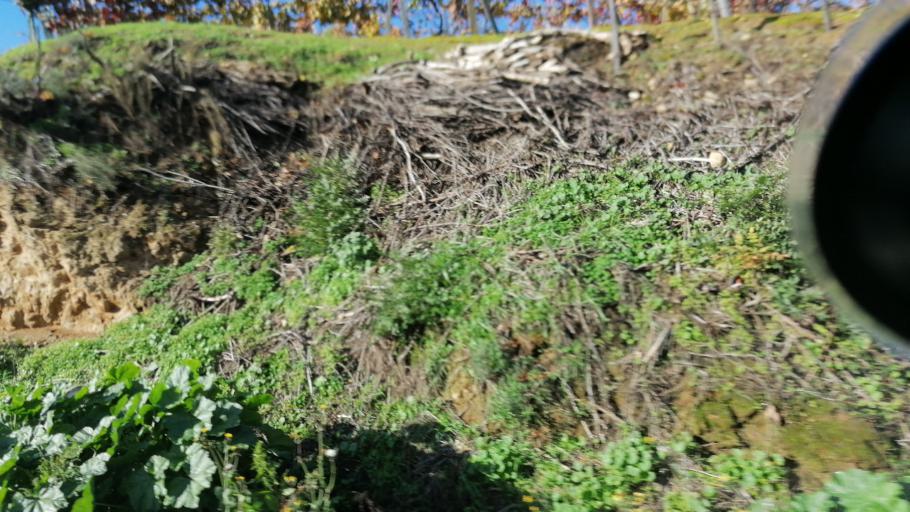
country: PT
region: Viseu
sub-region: Lamego
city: Lamego
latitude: 41.1261
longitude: -7.7849
